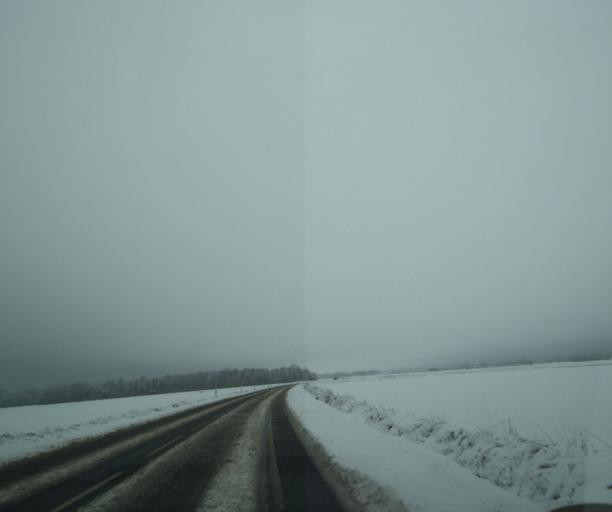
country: FR
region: Champagne-Ardenne
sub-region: Departement de la Haute-Marne
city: Wassy
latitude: 48.5657
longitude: 4.9215
